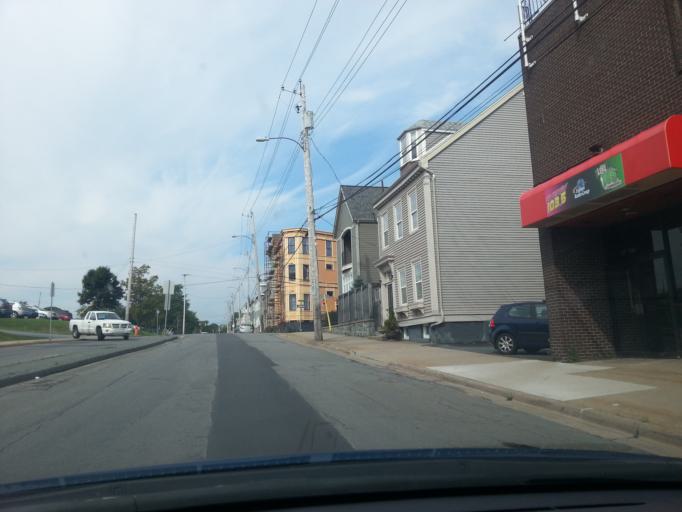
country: CA
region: Nova Scotia
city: Halifax
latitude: 44.6504
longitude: -63.5818
